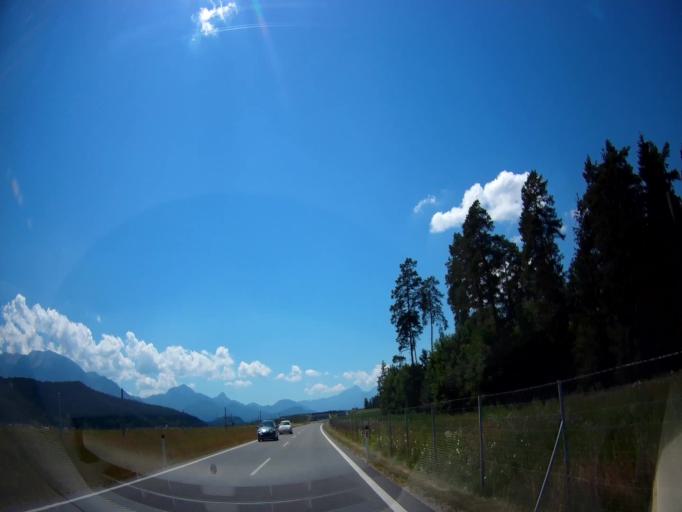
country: AT
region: Carinthia
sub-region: Politischer Bezirk Volkermarkt
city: Bleiburg/Pliberk
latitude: 46.6083
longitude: 14.7795
